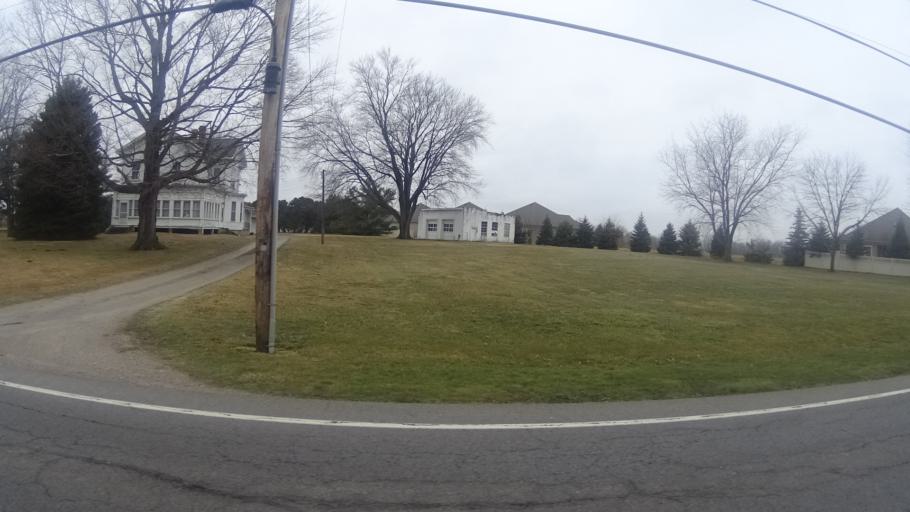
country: US
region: Ohio
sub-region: Erie County
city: Sandusky
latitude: 41.4231
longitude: -82.6542
